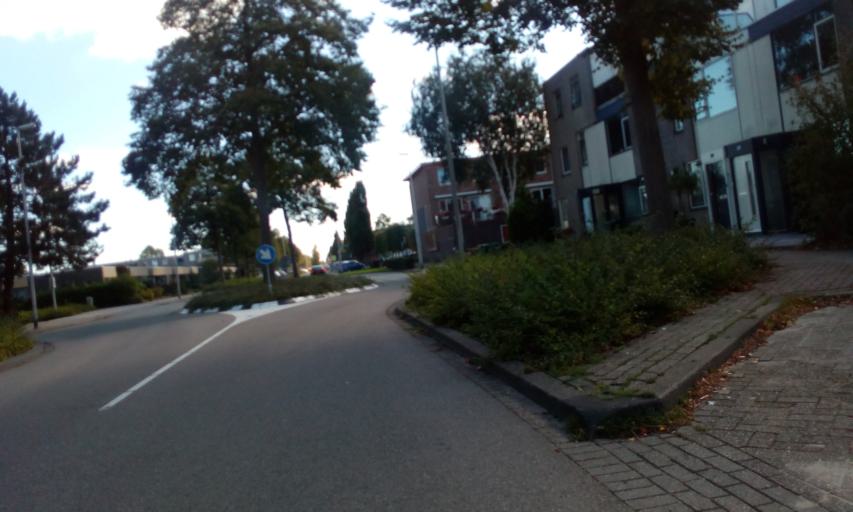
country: NL
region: South Holland
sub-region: Gemeente Rijnwoude
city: Benthuizen
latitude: 52.0757
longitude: 4.5176
